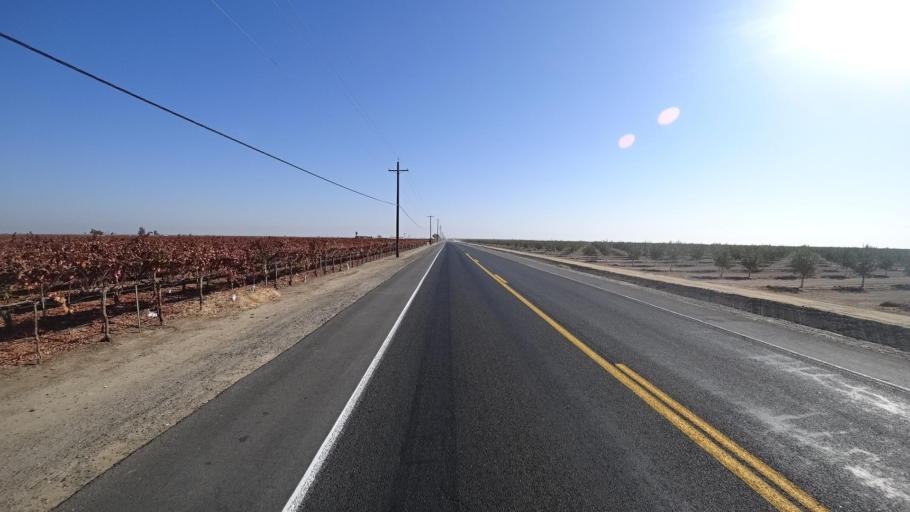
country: US
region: California
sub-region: Kern County
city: Delano
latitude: 35.7178
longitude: -119.3024
